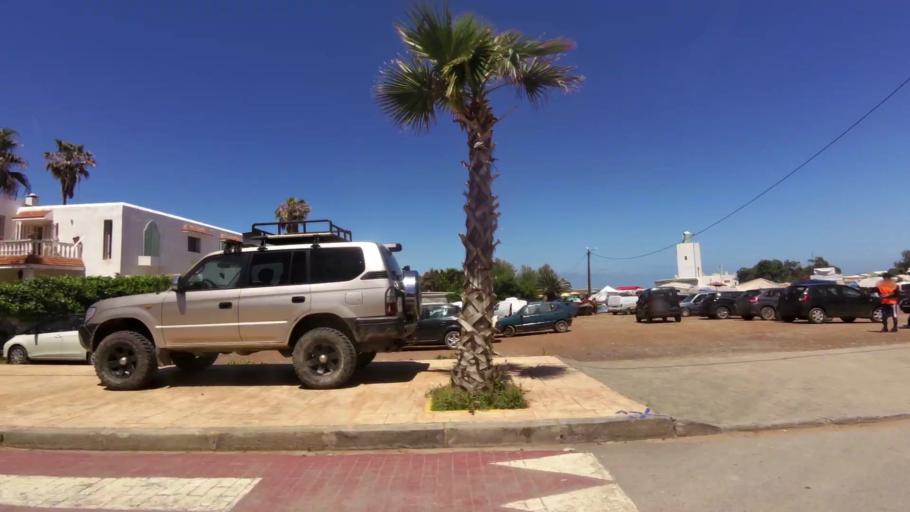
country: MA
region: Grand Casablanca
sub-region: Nouaceur
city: Dar Bouazza
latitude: 33.5264
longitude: -7.8174
